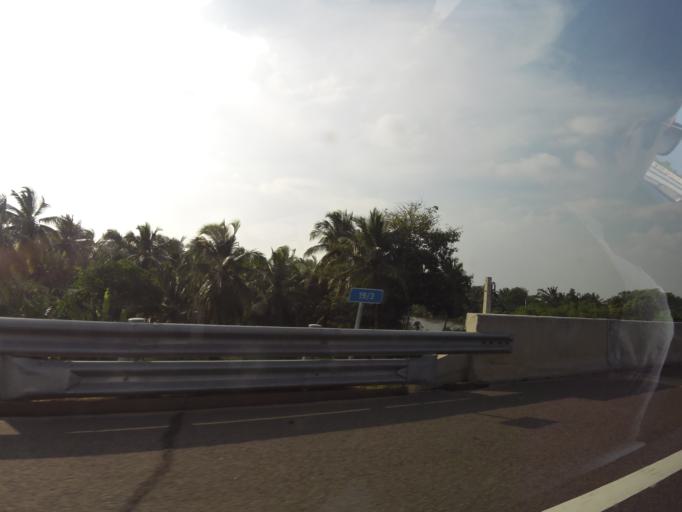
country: LK
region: Western
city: Ja Ela
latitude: 7.1066
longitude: 79.8776
